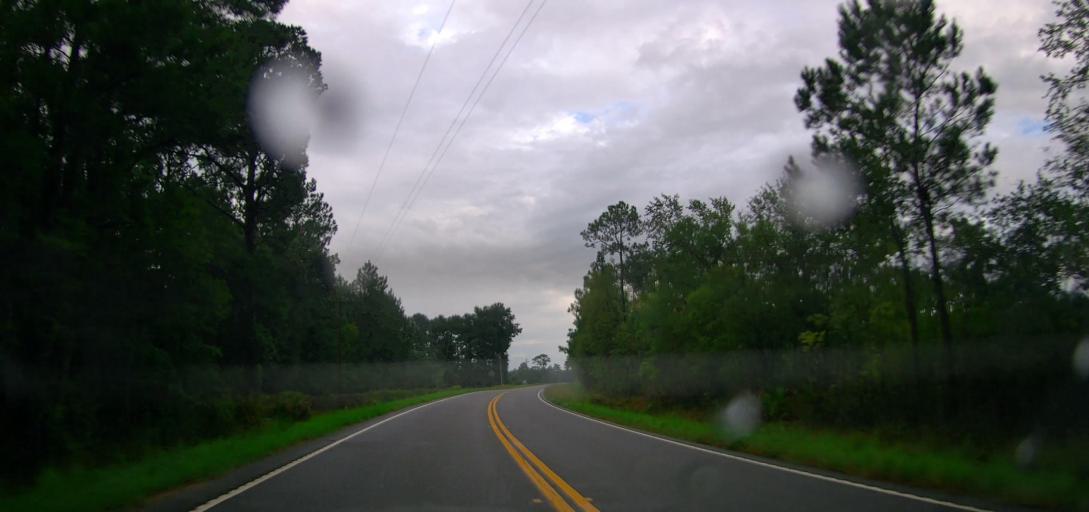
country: US
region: Georgia
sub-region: Ware County
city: Deenwood
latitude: 31.2774
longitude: -82.4193
